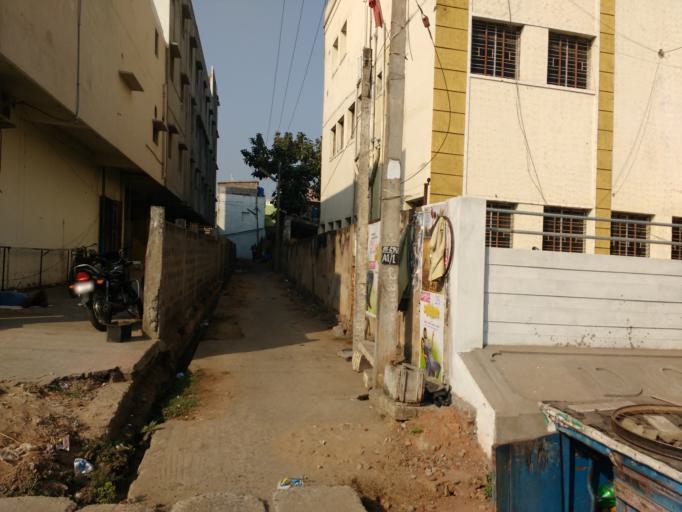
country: IN
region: Andhra Pradesh
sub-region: Srikakulam
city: Srikakulam
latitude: 18.2949
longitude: 83.8993
